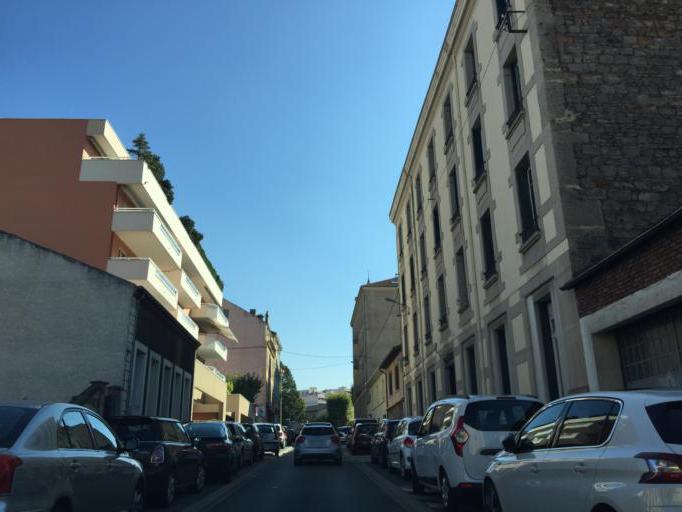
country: FR
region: Rhone-Alpes
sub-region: Departement de la Loire
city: Saint-Chamond
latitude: 45.4742
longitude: 4.5162
